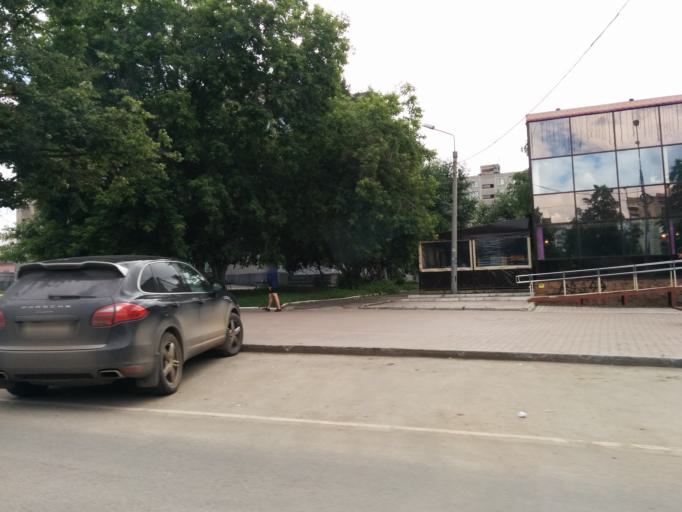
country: RU
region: Perm
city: Perm
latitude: 58.0084
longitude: 56.2233
